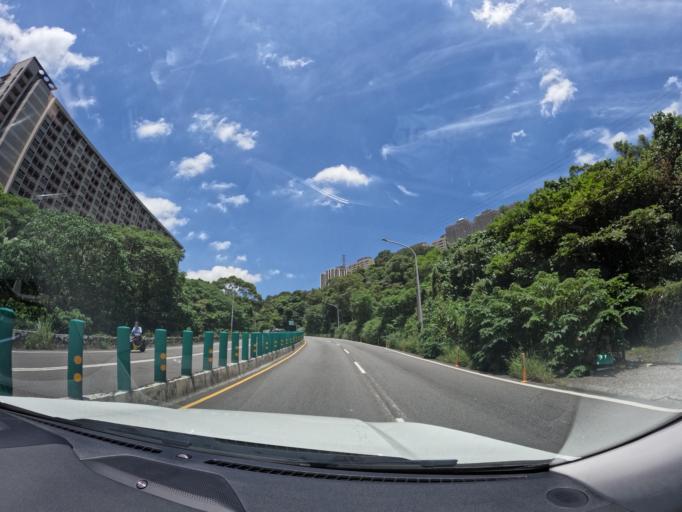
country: TW
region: Taipei
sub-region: Taipei
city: Banqiao
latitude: 25.0359
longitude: 121.3914
